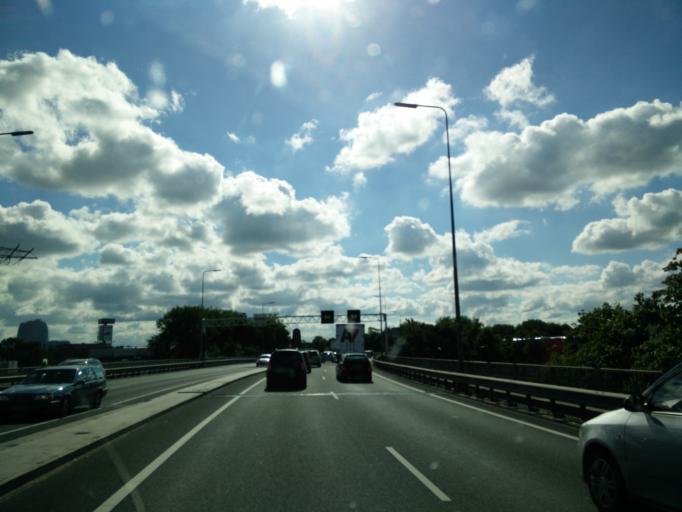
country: NL
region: Groningen
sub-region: Gemeente Groningen
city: Oosterpark
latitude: 53.2134
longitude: 6.5961
